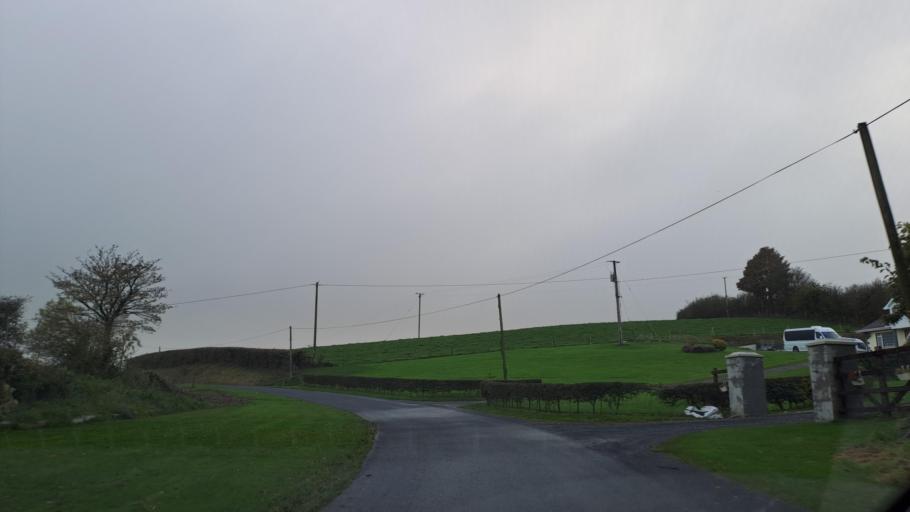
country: IE
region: Ulster
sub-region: An Cabhan
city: Kingscourt
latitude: 53.9700
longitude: -6.7888
